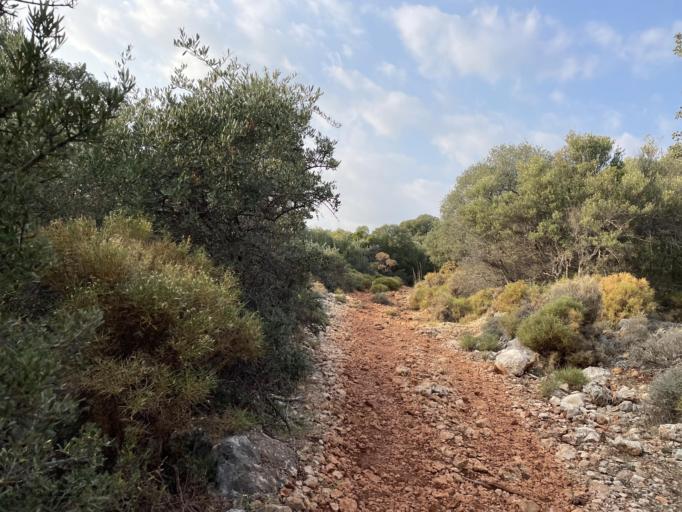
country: TR
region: Antalya
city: Kas
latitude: 36.1624
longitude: 29.6550
